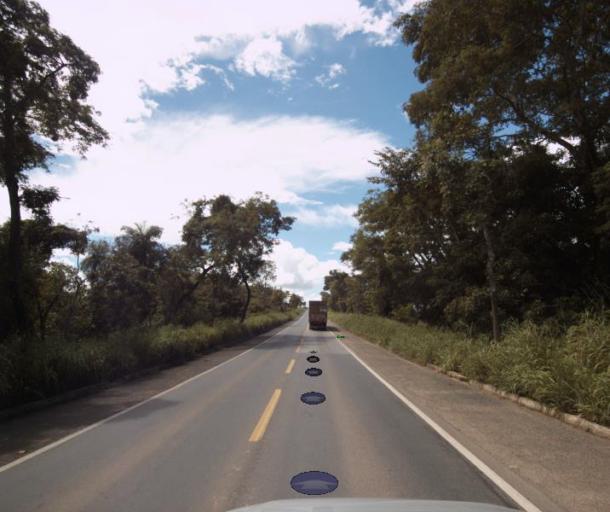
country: BR
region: Goias
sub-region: Uruacu
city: Uruacu
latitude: -14.1266
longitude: -49.1097
